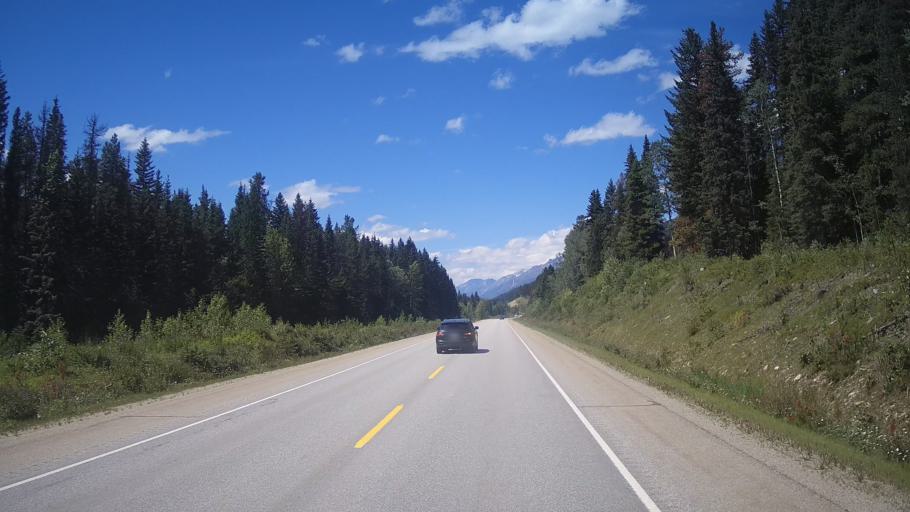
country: CA
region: Alberta
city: Jasper Park Lodge
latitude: 52.8723
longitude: -118.6844
